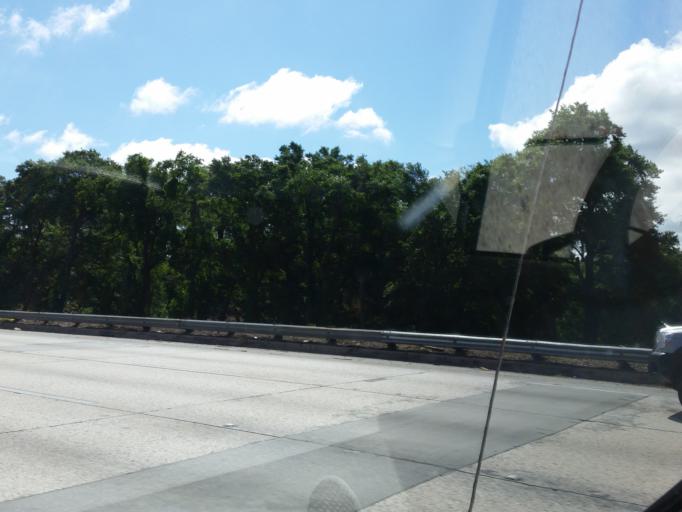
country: US
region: Florida
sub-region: Orange County
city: Holden Heights
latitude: 28.5137
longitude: -81.3915
